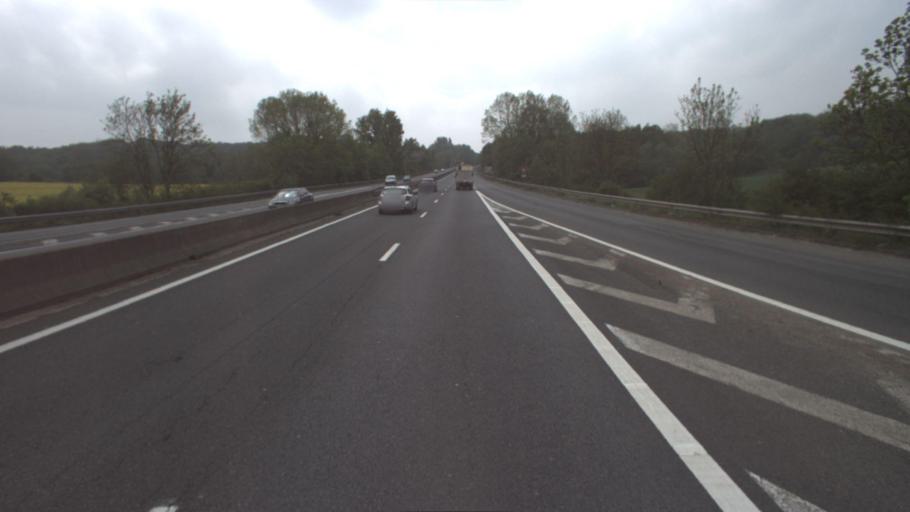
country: FR
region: Ile-de-France
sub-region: Departement de Seine-et-Marne
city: Saint-Mard
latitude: 49.0558
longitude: 2.7002
